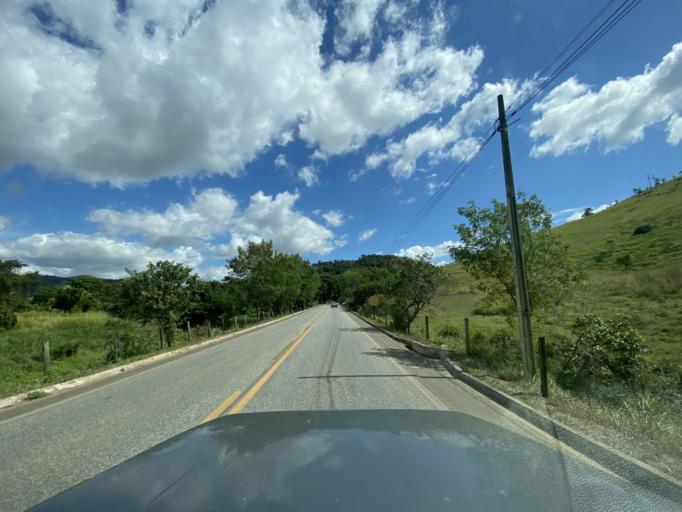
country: BR
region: Espirito Santo
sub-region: Jeronimo Monteiro
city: Jeronimo Monteiro
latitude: -20.7687
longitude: -41.4408
